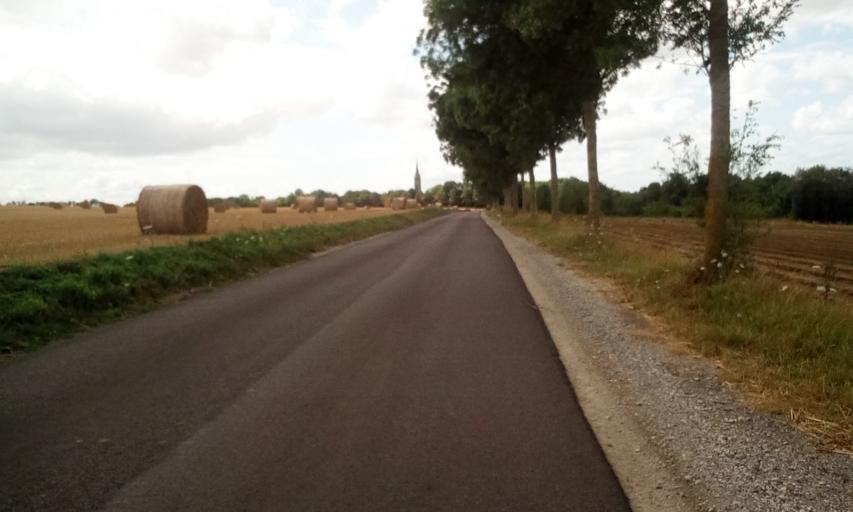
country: FR
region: Lower Normandy
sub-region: Departement du Calvados
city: Courseulles-sur-Mer
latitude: 49.2948
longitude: -0.4804
